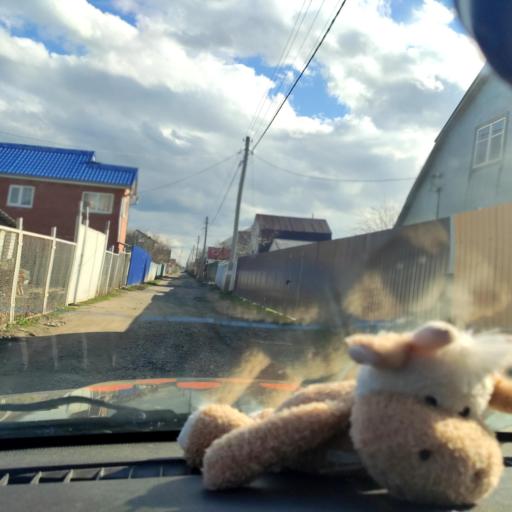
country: RU
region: Samara
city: Tol'yatti
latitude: 53.5951
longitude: 49.3088
